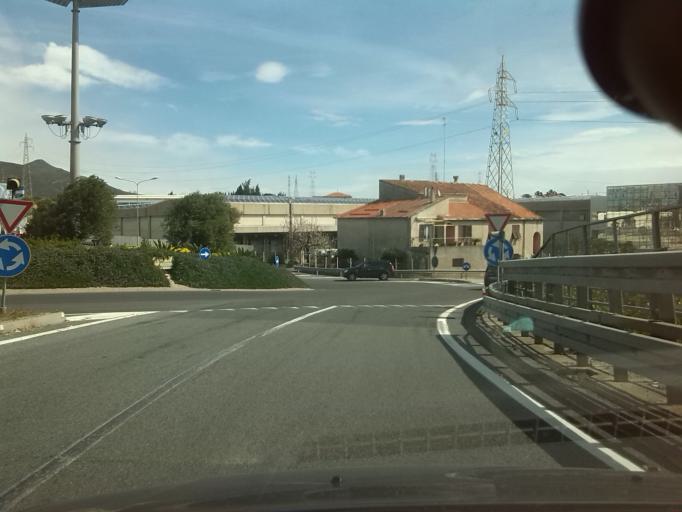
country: IT
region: Liguria
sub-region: Provincia di Savona
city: San Fedele-Lusignano
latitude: 44.0682
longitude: 8.1701
